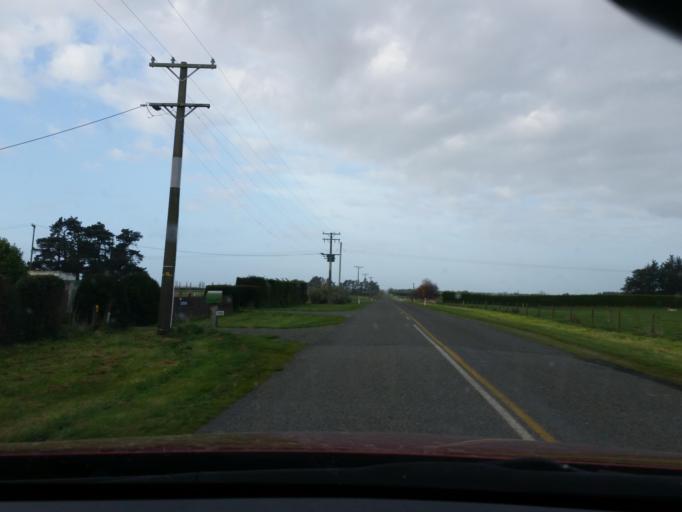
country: NZ
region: Southland
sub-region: Southland District
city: Winton
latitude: -46.2664
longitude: 168.3671
